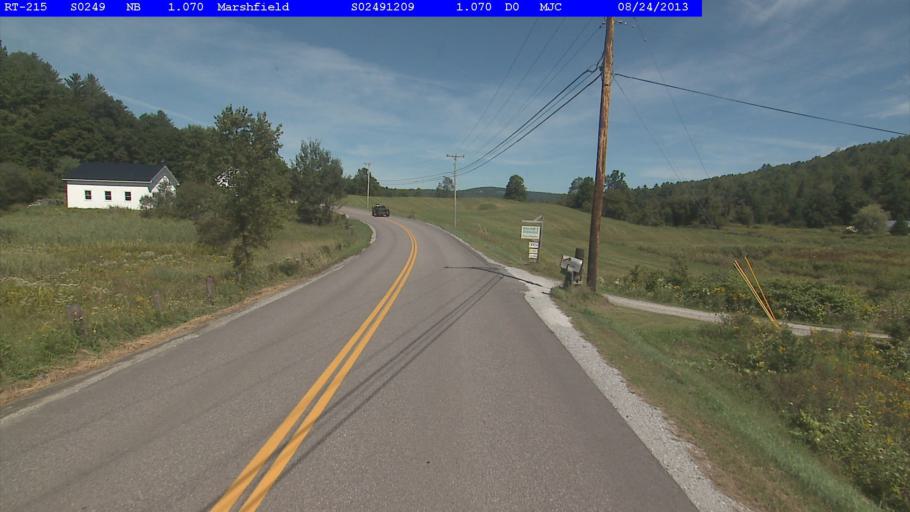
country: US
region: Vermont
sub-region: Caledonia County
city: Hardwick
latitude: 44.3631
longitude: -72.3363
